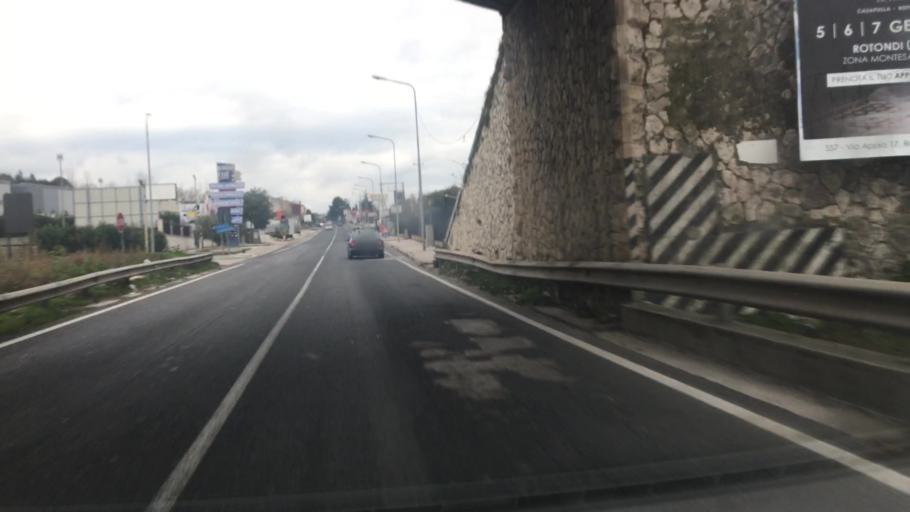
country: IT
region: Campania
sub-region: Provincia di Benevento
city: Arpaia
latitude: 41.0402
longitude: 14.5600
